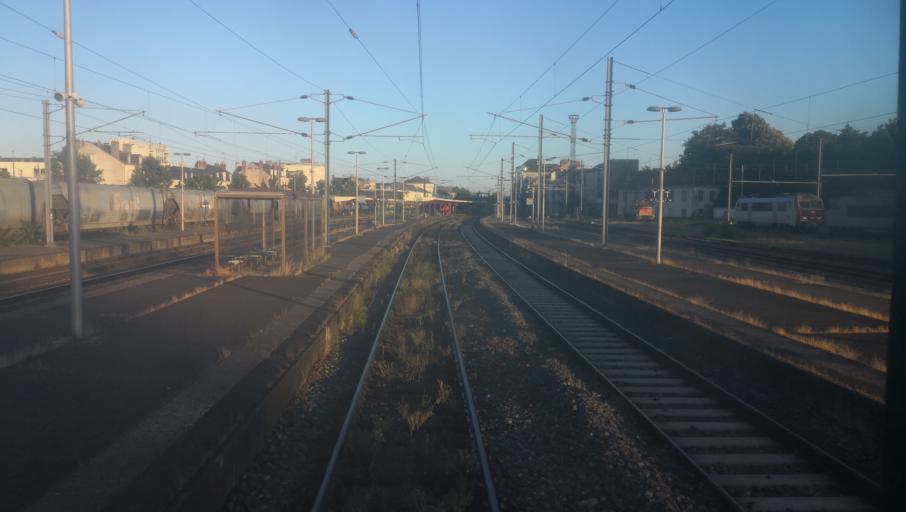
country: FR
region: Bourgogne
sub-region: Departement de la Nievre
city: Nevers
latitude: 46.9891
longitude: 3.1495
